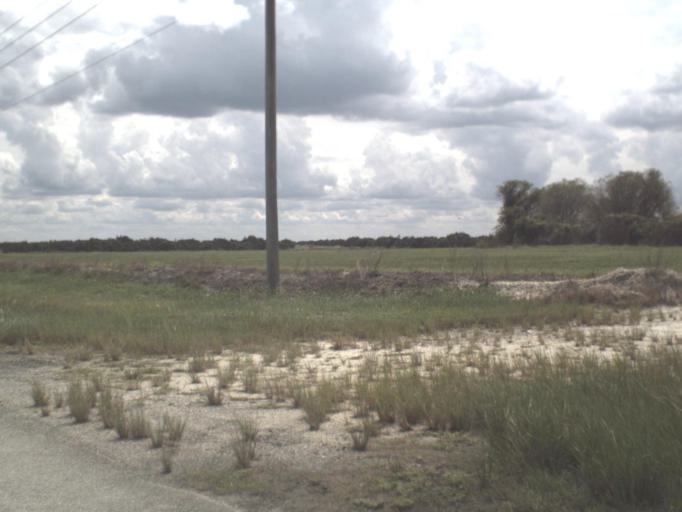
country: US
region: Florida
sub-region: DeSoto County
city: Nocatee
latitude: 27.0401
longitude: -81.7761
